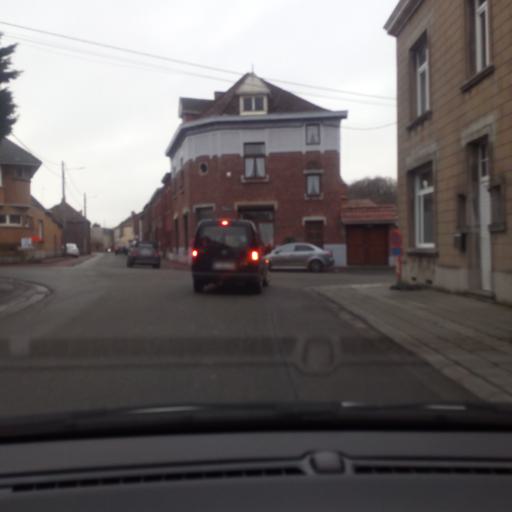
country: BE
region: Wallonia
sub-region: Province du Hainaut
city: Dour
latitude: 50.4000
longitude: 3.7737
